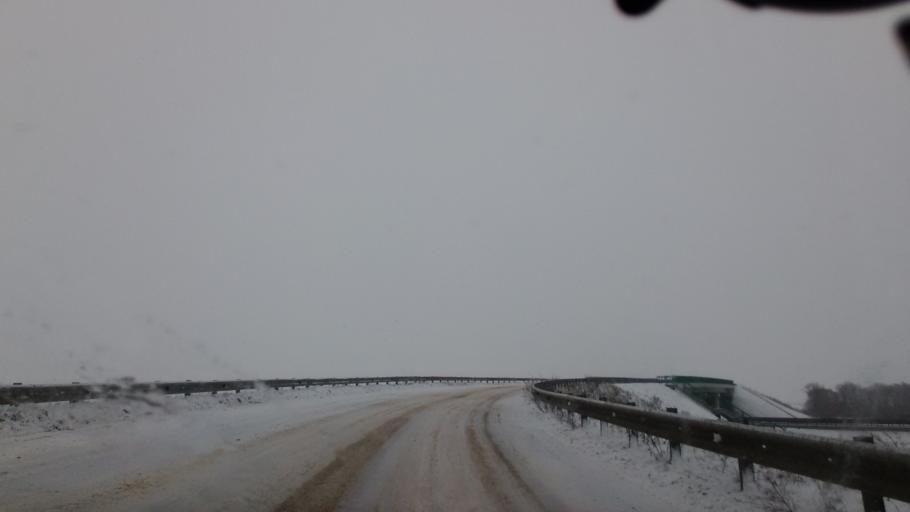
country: RU
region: Tula
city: Bogoroditsk
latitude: 53.7082
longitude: 38.0447
